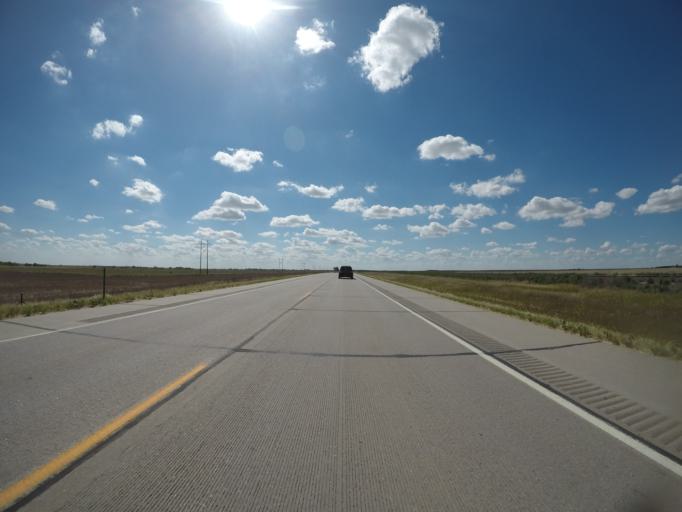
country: US
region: Colorado
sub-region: Phillips County
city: Holyoke
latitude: 40.5940
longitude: -102.3623
